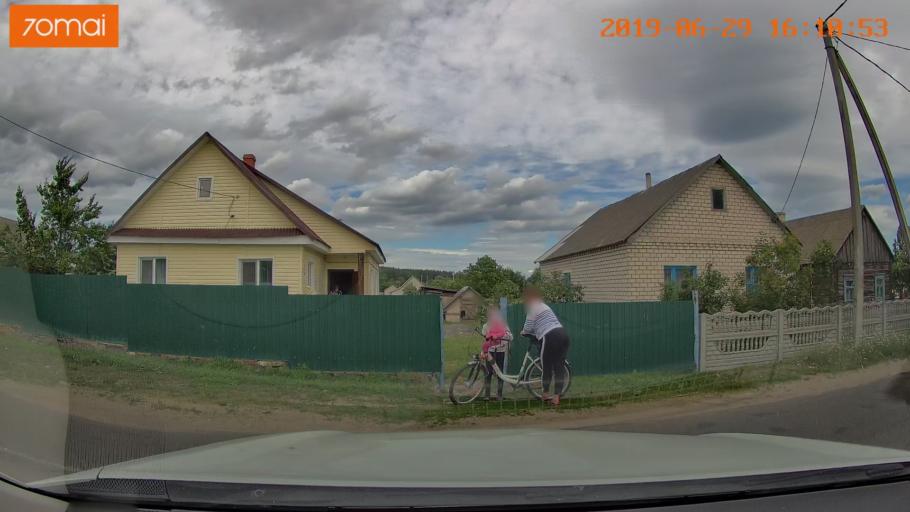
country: BY
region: Brest
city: Luninyets
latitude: 52.2045
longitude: 27.0112
